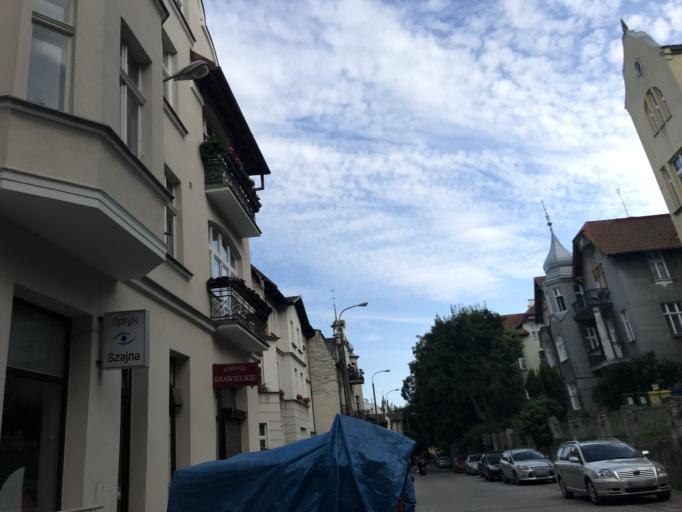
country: PL
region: Pomeranian Voivodeship
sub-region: Sopot
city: Sopot
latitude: 54.4431
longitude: 18.5648
